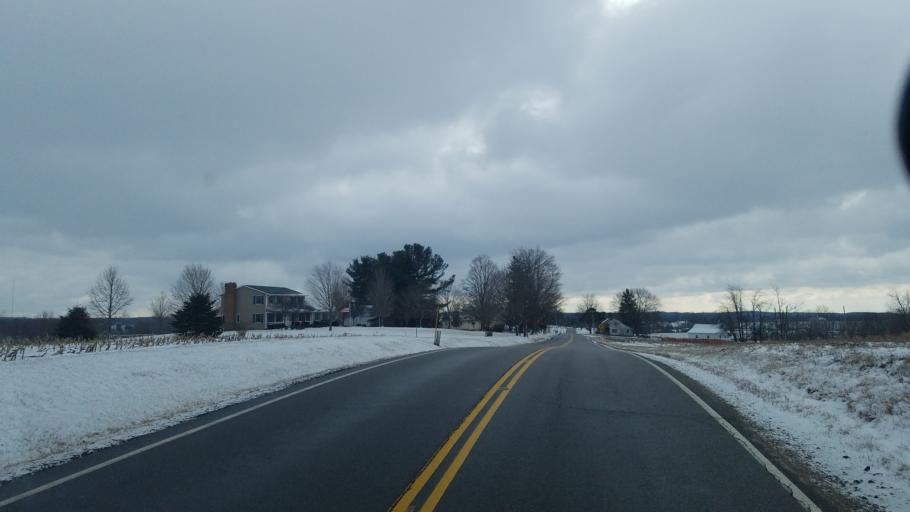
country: US
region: Ohio
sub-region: Knox County
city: Fredericktown
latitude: 40.5330
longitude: -82.5586
